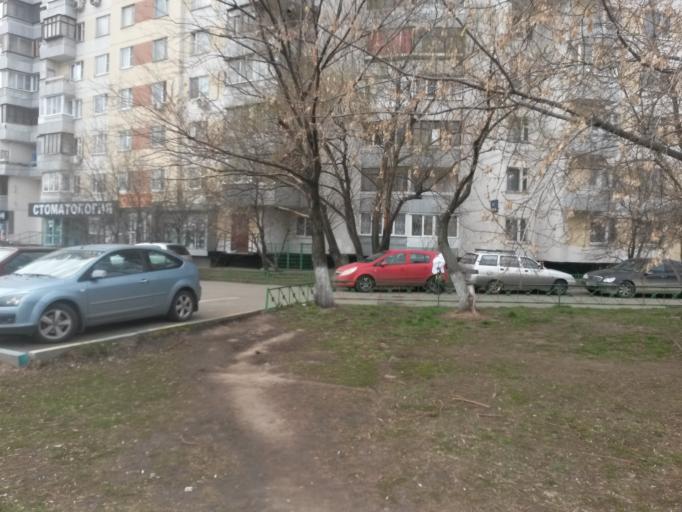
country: RU
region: Moscow
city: Brateyevo
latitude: 55.6497
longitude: 37.7424
